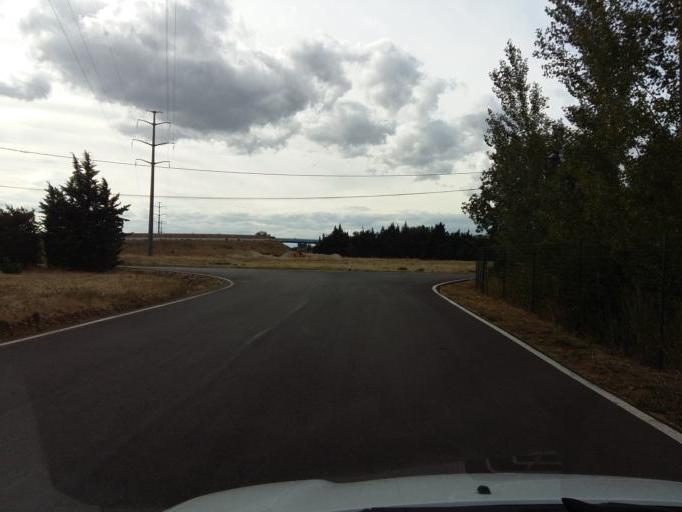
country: FR
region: Provence-Alpes-Cote d'Azur
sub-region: Departement du Vaucluse
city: Carpentras
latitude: 44.0366
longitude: 5.0341
